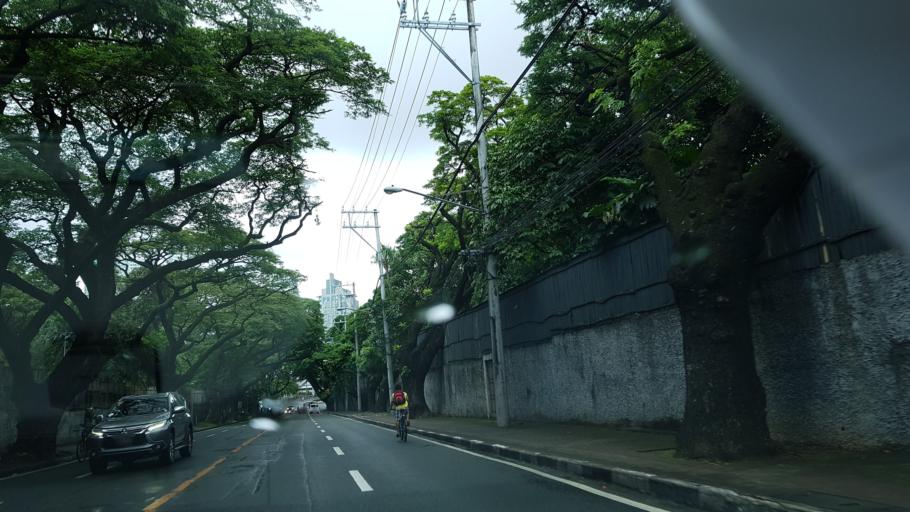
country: PH
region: Metro Manila
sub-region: Makati City
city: Makati City
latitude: 14.5487
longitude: 121.0321
